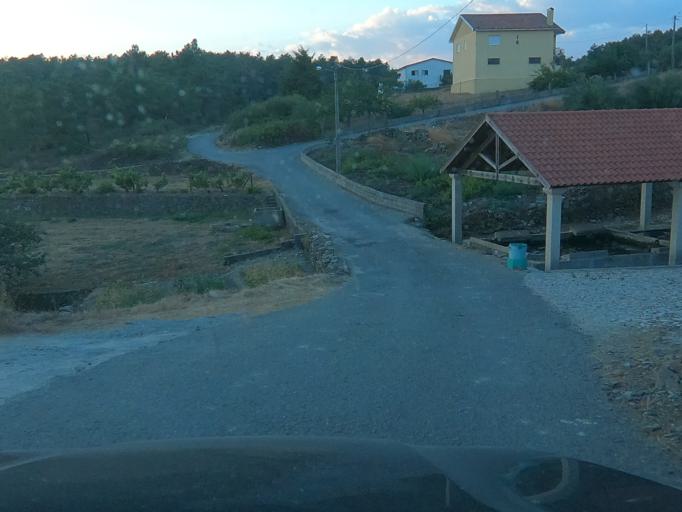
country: PT
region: Vila Real
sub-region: Sabrosa
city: Vilela
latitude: 41.2240
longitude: -7.6051
